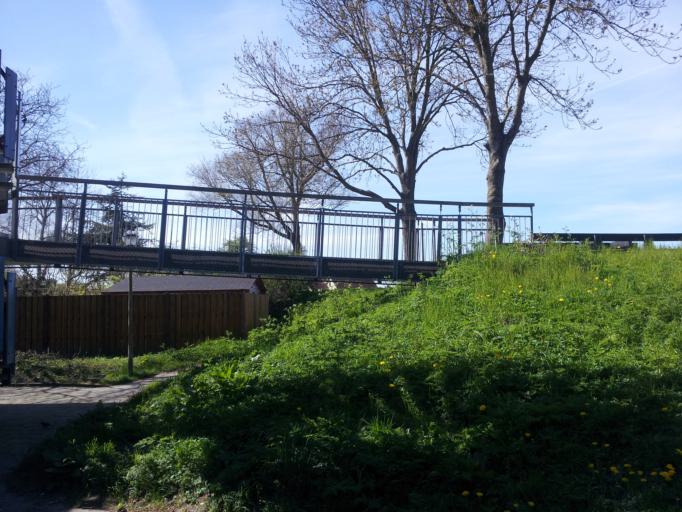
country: NL
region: South Holland
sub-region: Gemeente Zoetermeer
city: Zoetermeer
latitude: 52.0704
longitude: 4.4740
